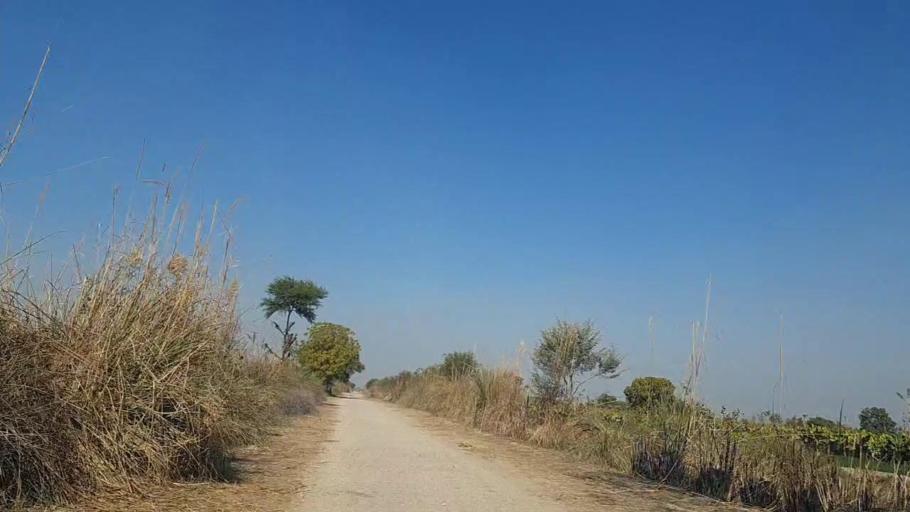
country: PK
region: Sindh
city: Sakrand
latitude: 26.2530
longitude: 68.2207
